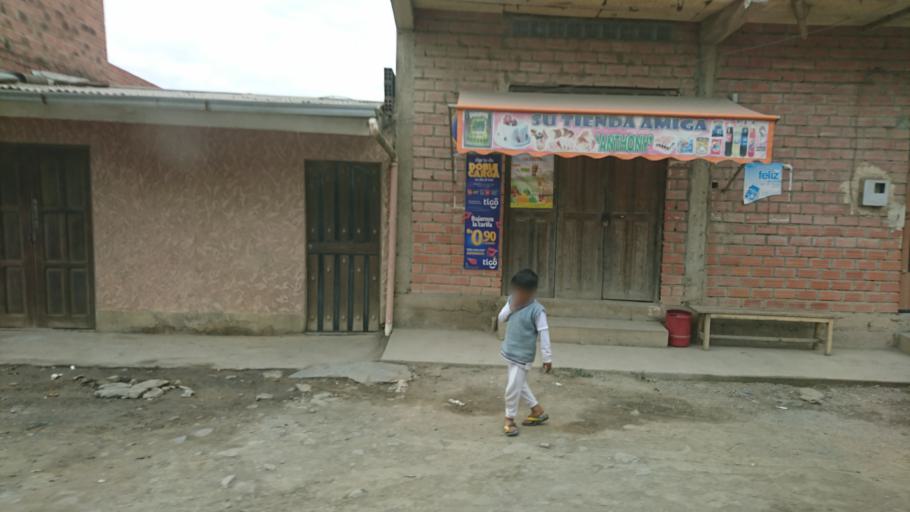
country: BO
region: La Paz
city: Coroico
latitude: -16.2005
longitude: -67.6975
